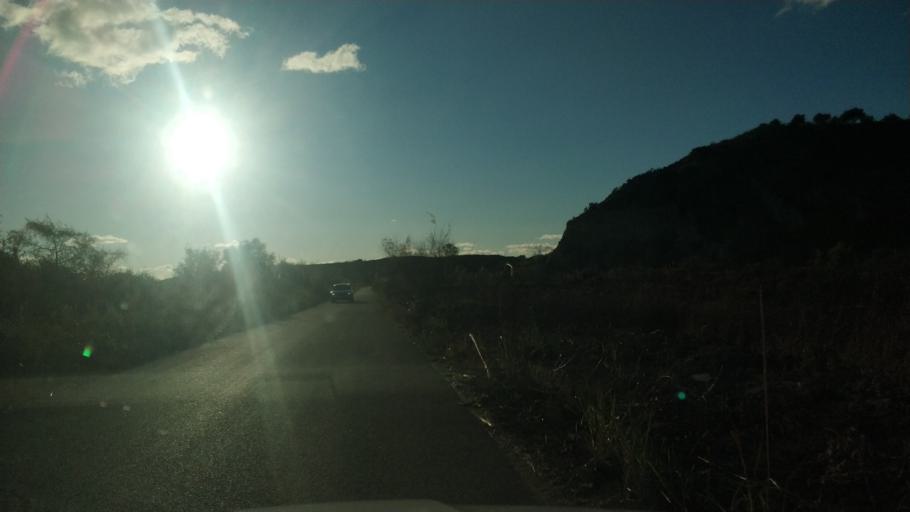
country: AL
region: Vlore
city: Vlore
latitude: 40.5052
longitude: 19.4223
